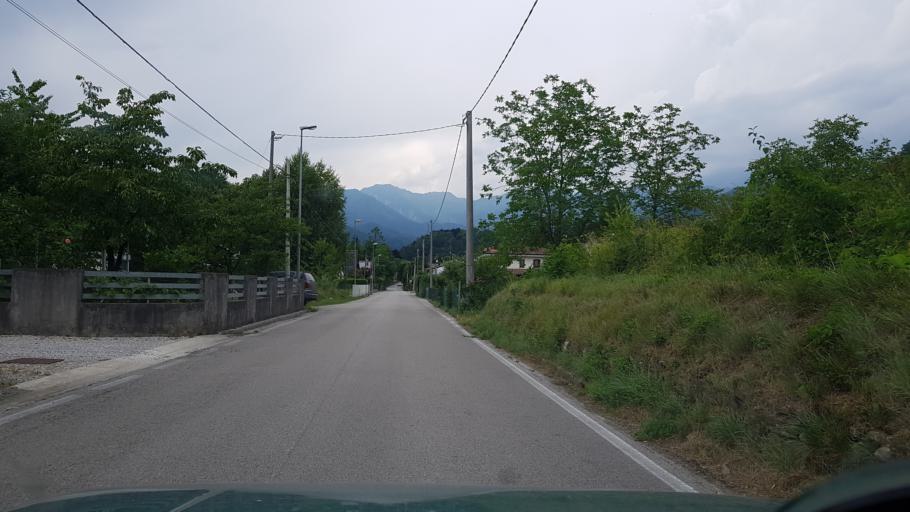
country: IT
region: Friuli Venezia Giulia
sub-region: Provincia di Udine
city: Tarcento
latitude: 46.2112
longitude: 13.2284
